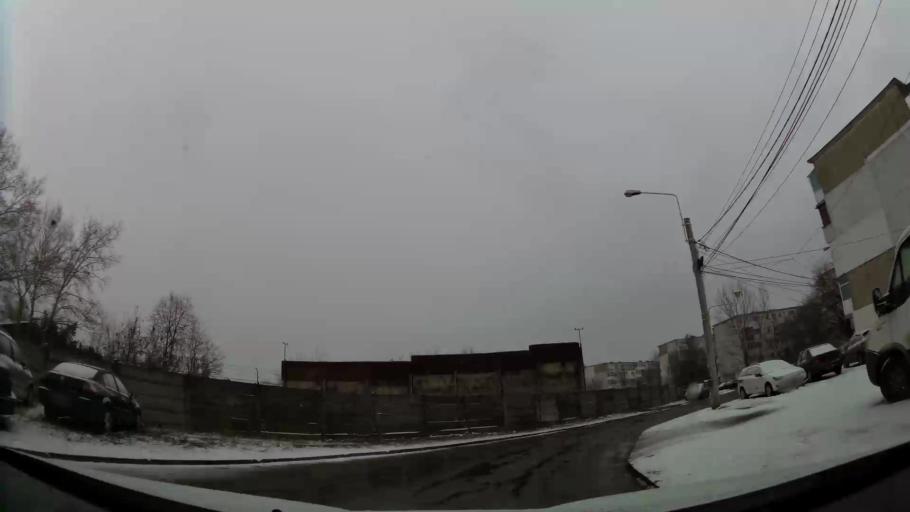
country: RO
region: Prahova
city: Ploiesti
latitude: 44.9342
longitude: 25.9943
